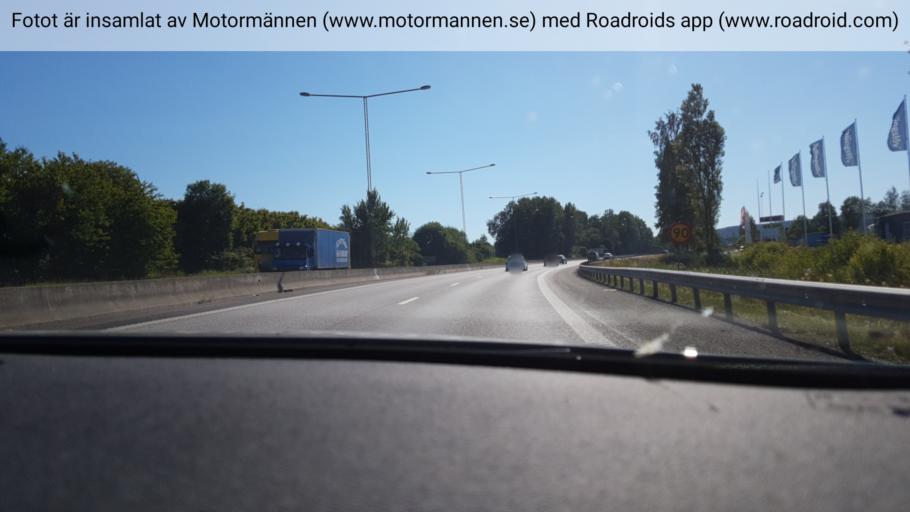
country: SE
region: Joenkoeping
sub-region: Jonkopings Kommun
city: Jonkoping
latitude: 57.7604
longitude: 14.1809
